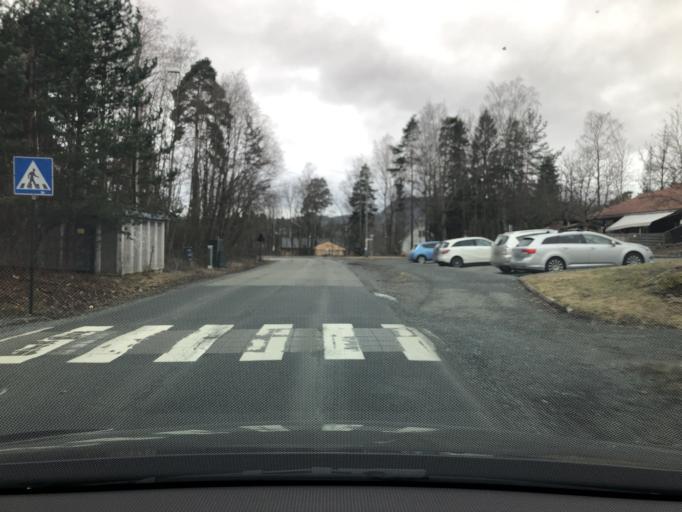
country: NO
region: Akershus
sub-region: Baerum
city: Sandvika
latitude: 59.8693
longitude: 10.5157
